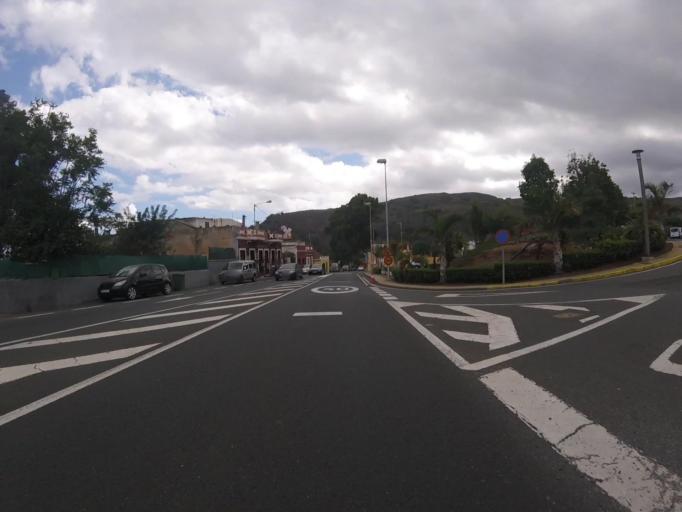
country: ES
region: Canary Islands
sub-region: Provincia de Las Palmas
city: Santa Brigida
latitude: 28.0274
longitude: -15.5056
